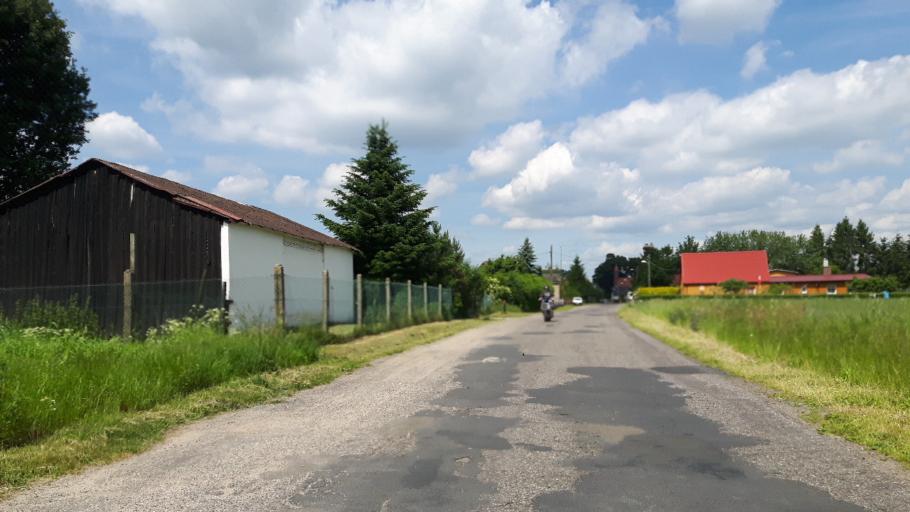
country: PL
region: West Pomeranian Voivodeship
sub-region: Powiat goleniowski
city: Osina
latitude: 53.6763
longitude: 14.9999
